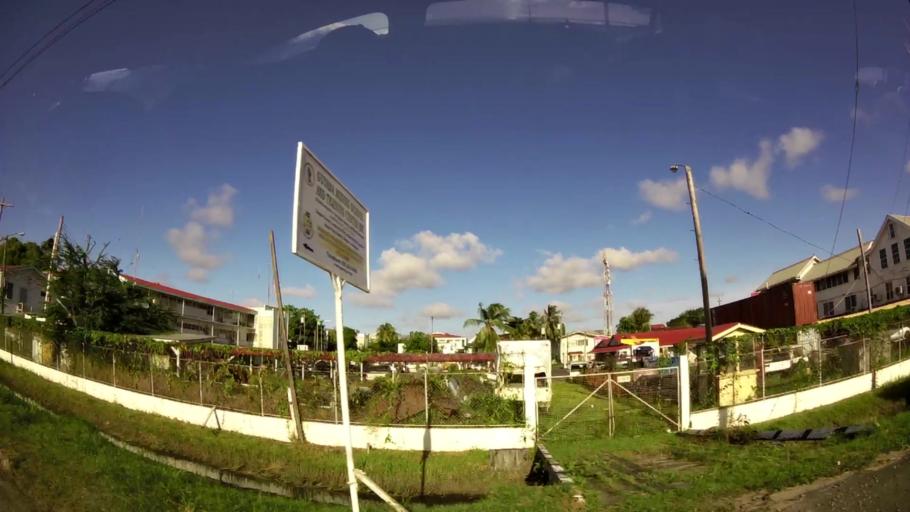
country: GY
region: Demerara-Mahaica
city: Georgetown
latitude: 6.8243
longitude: -58.1642
